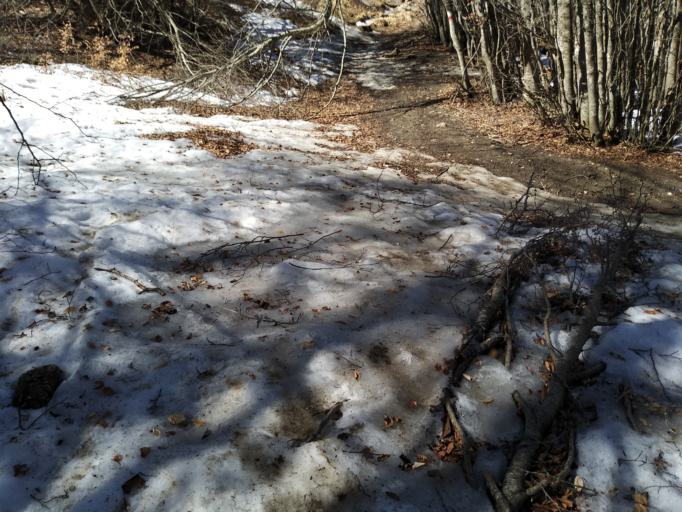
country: IT
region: Emilia-Romagna
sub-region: Provincia di Reggio Emilia
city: Collagna
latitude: 44.3776
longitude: 10.2828
